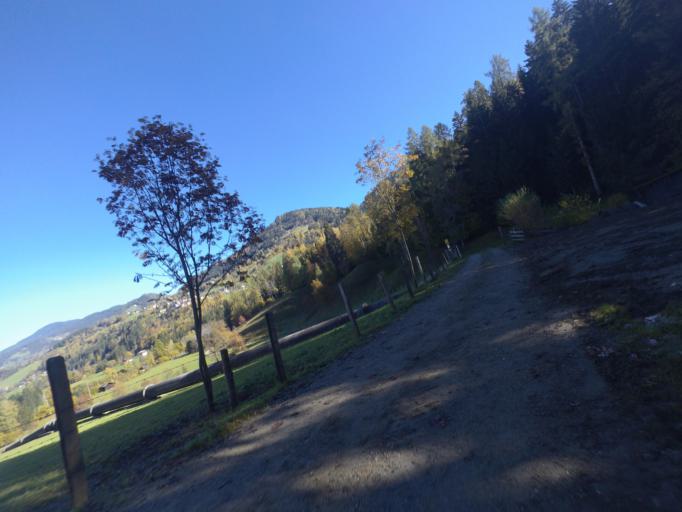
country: AT
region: Salzburg
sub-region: Politischer Bezirk Sankt Johann im Pongau
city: Schwarzach im Pongau
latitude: 47.3184
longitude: 13.1833
